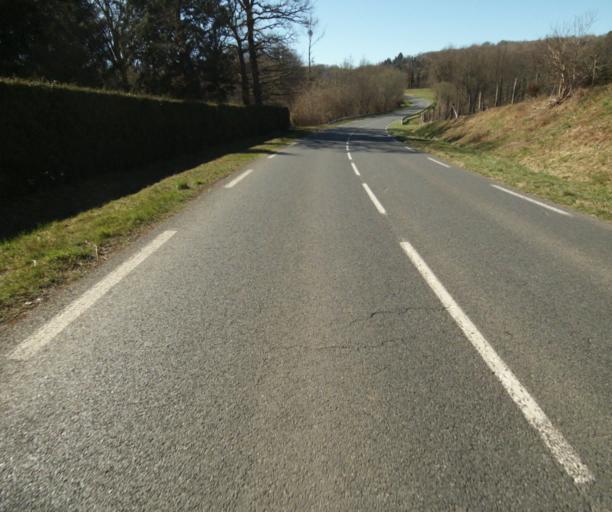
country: FR
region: Limousin
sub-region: Departement de la Correze
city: Chamboulive
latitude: 45.4194
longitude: 1.7147
